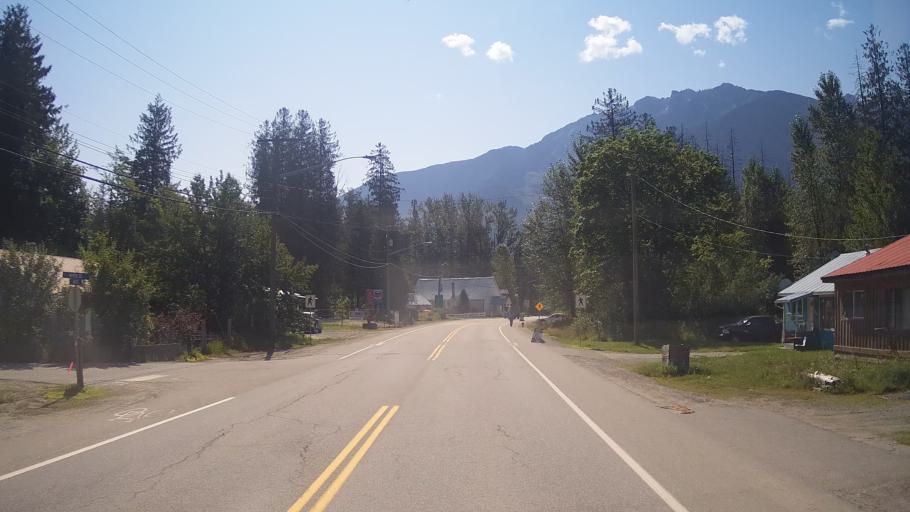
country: CA
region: British Columbia
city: Pemberton
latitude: 50.3173
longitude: -122.7189
